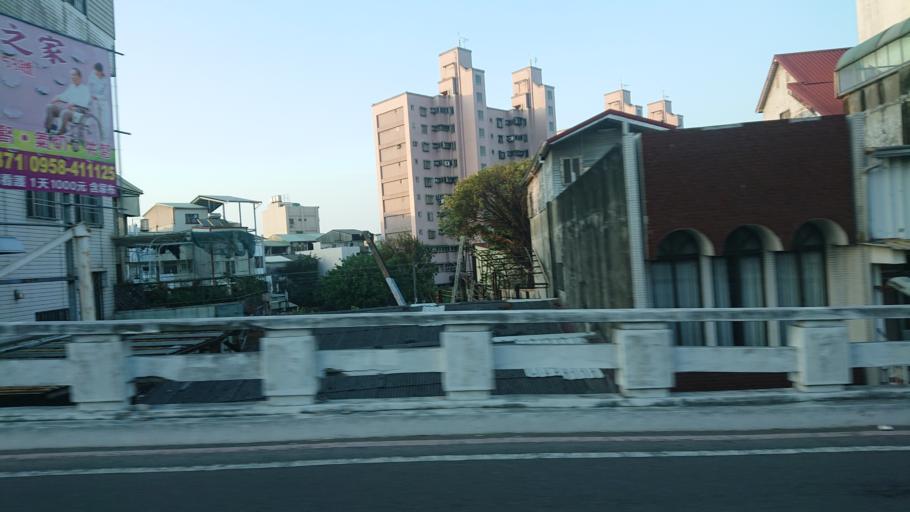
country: TW
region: Taiwan
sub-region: Tainan
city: Tainan
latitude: 23.0060
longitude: 120.2151
